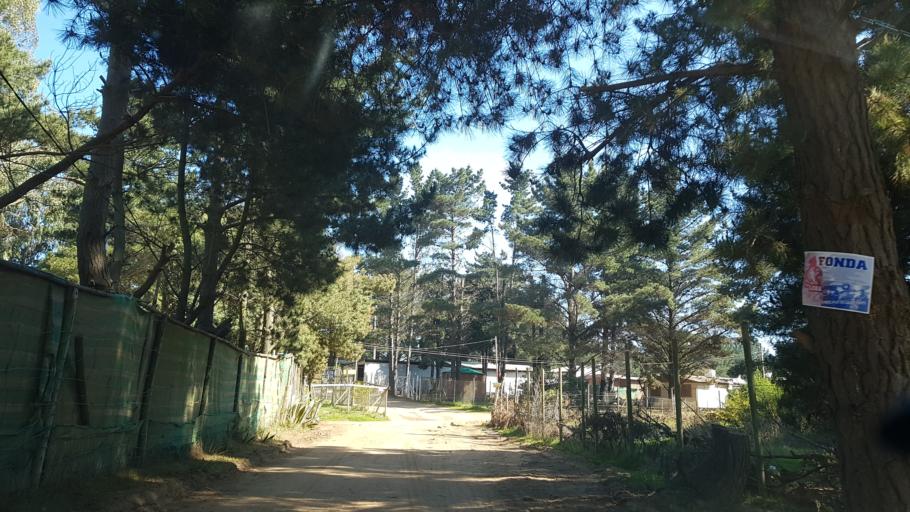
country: CL
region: Valparaiso
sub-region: Provincia de Valparaiso
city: Valparaiso
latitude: -33.1233
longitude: -71.6695
